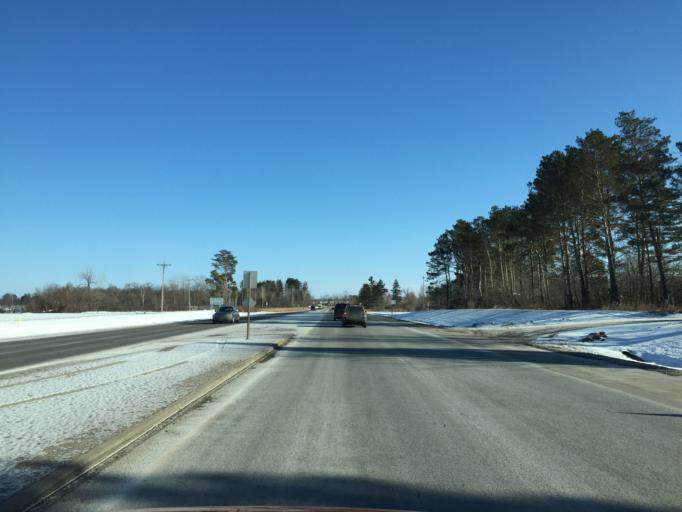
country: US
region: Minnesota
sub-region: Isanti County
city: Cambridge
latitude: 45.5729
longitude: -93.1916
